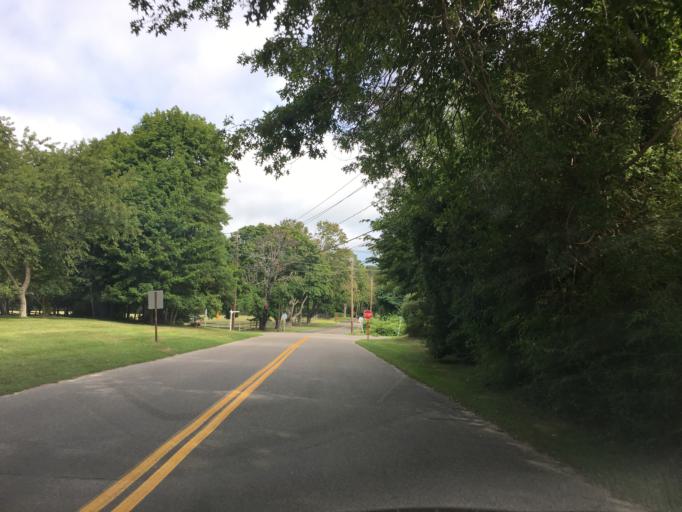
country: US
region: New York
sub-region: Suffolk County
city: Shelter Island Heights
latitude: 41.0576
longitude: -72.3691
